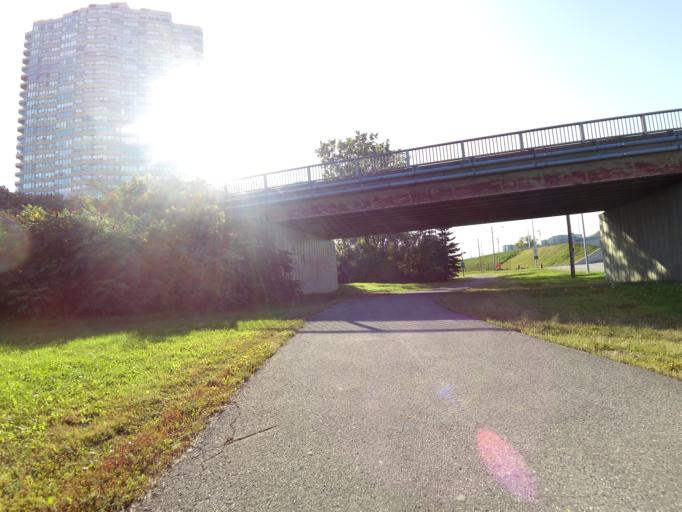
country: CA
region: Ontario
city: Ottawa
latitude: 45.4121
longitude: -75.6599
